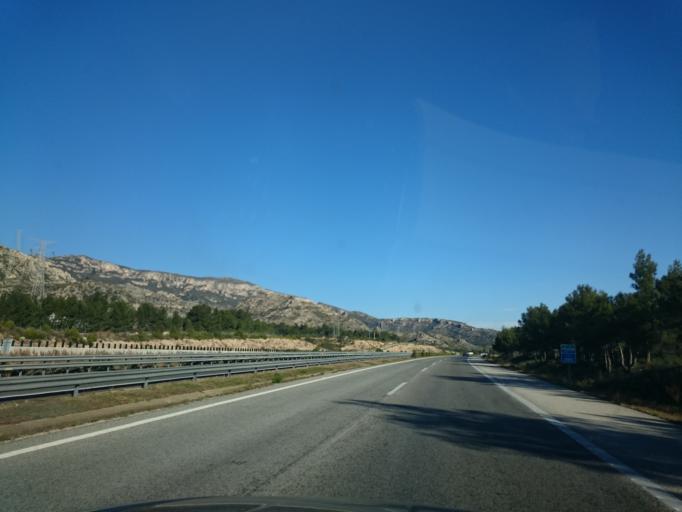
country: ES
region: Catalonia
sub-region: Provincia de Tarragona
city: l'Ametlla de Mar
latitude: 40.9747
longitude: 0.8802
